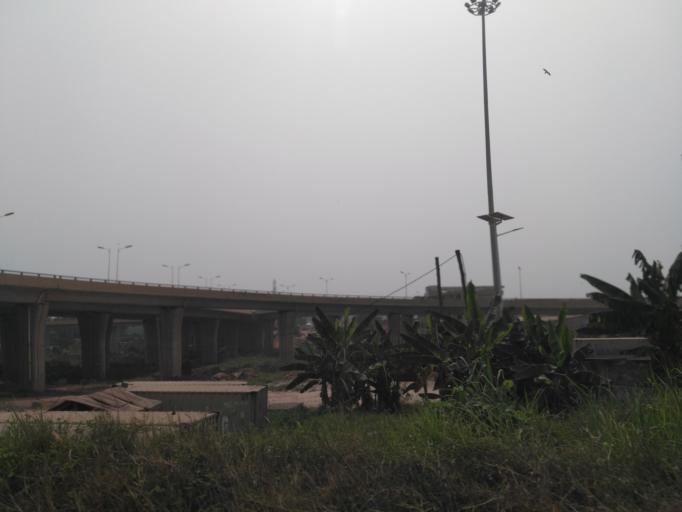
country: GH
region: Ashanti
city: Kumasi
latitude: 6.7002
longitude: -1.6460
